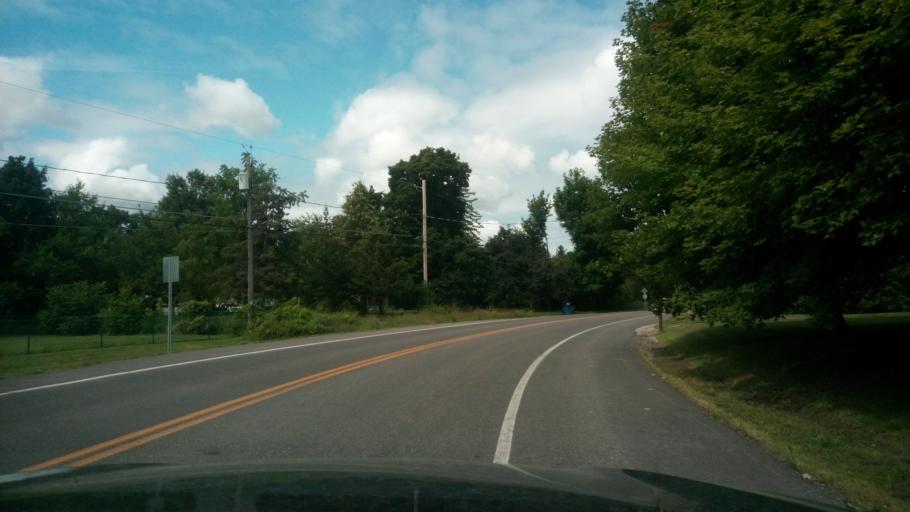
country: US
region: New York
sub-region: Onondaga County
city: East Syracuse
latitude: 43.0038
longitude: -76.0800
